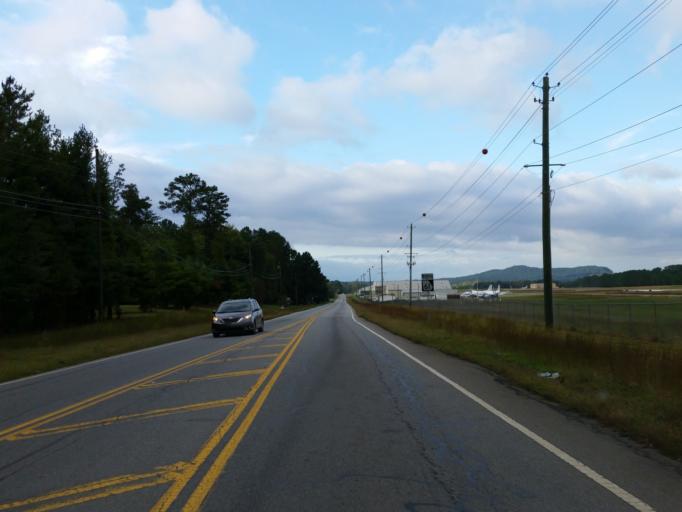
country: US
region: Georgia
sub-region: Bartow County
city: Cartersville
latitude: 34.1140
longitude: -84.8513
